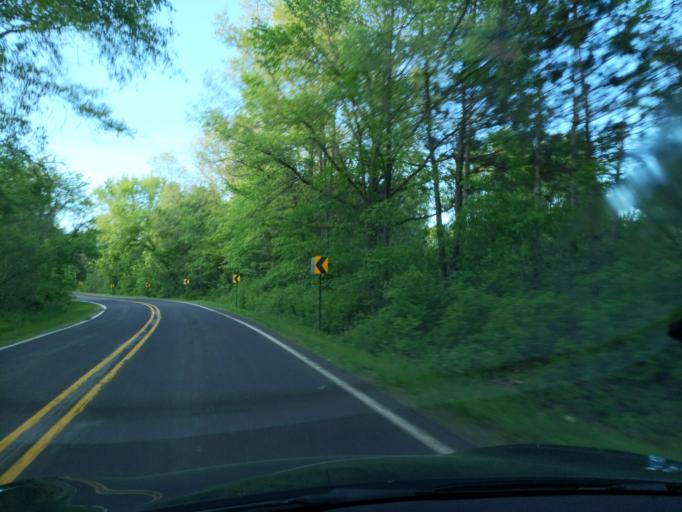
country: US
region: Michigan
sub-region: Ingham County
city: Leslie
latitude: 42.4941
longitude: -84.3163
